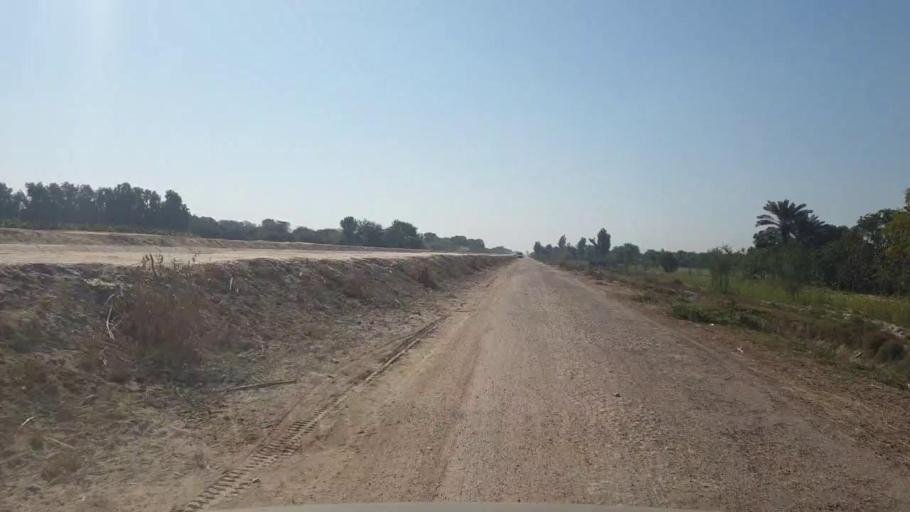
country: PK
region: Sindh
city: Mirwah Gorchani
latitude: 25.3000
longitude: 69.1030
